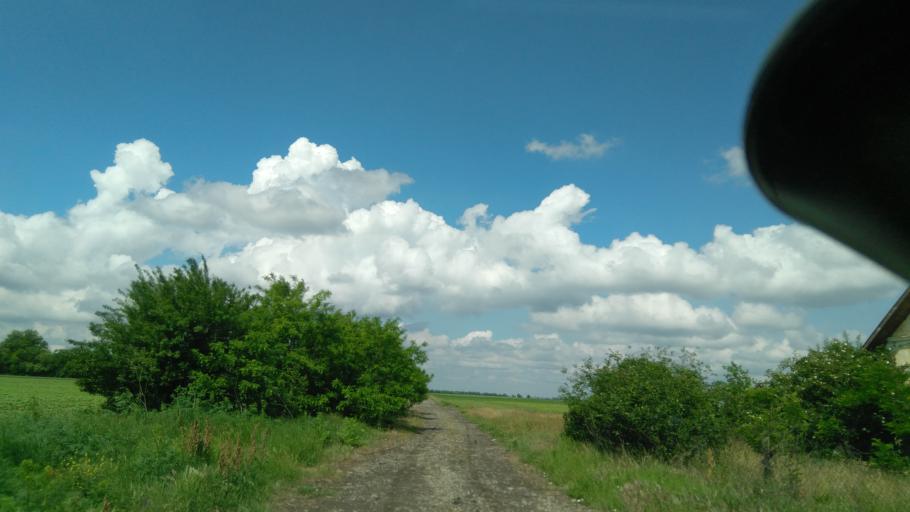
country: HU
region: Bekes
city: Mezobereny
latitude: 46.8336
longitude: 21.0136
